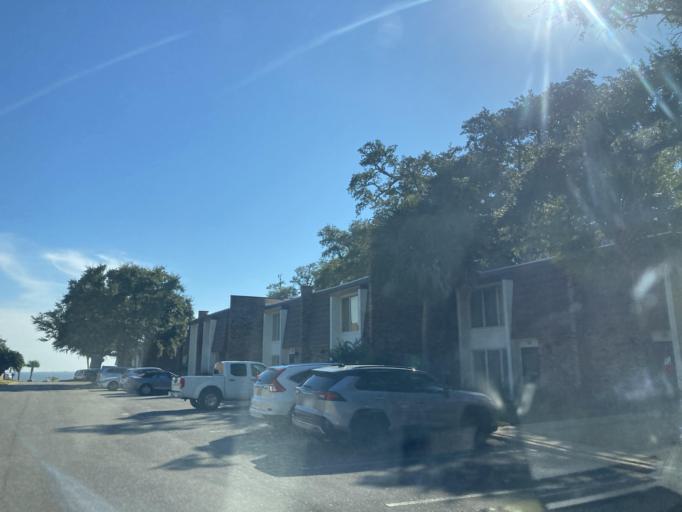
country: US
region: Mississippi
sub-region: Jackson County
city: Ocean Springs
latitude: 30.4050
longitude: -88.8261
